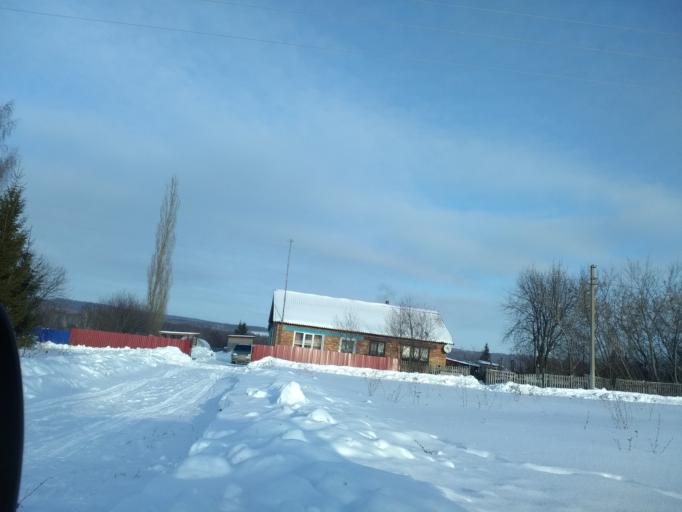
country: RU
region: Bashkortostan
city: Iglino
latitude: 54.6088
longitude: 56.4935
